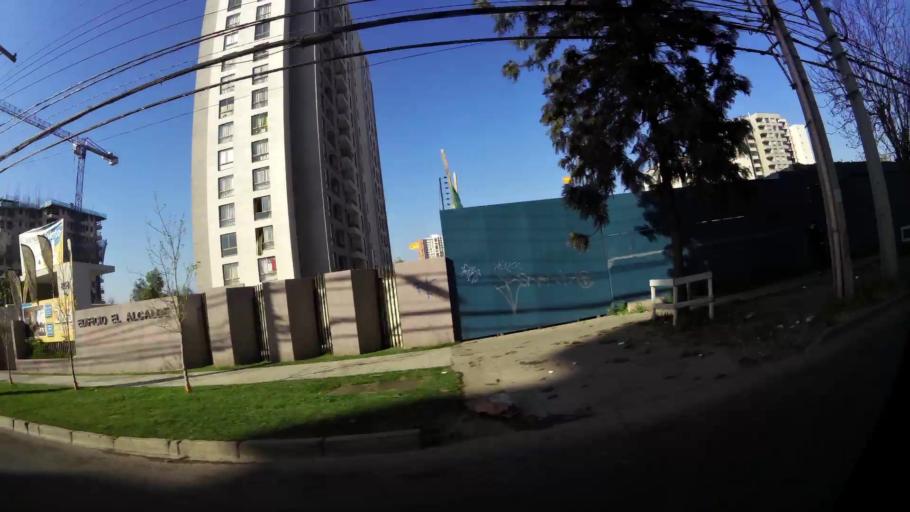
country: CL
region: Santiago Metropolitan
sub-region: Provincia de Santiago
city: Santiago
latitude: -33.4869
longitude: -70.6464
